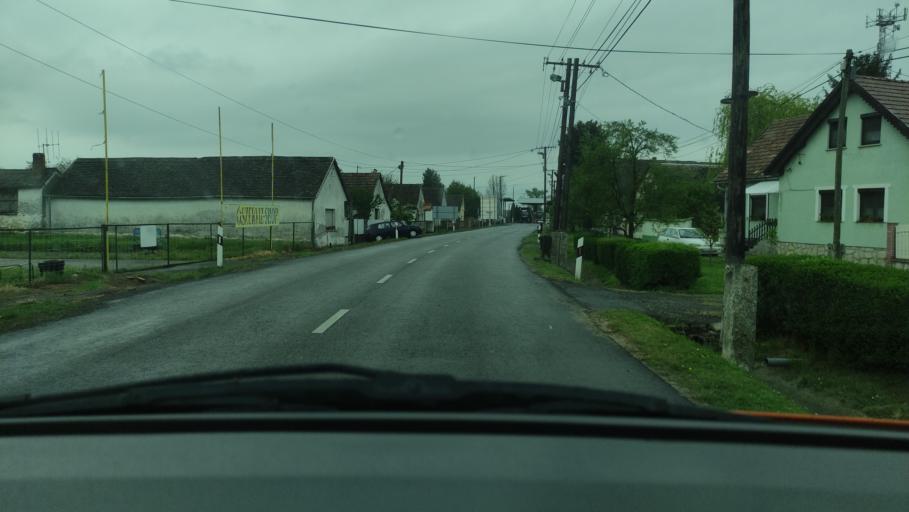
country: HU
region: Baranya
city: Mohacs
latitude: 45.8978
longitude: 18.6611
